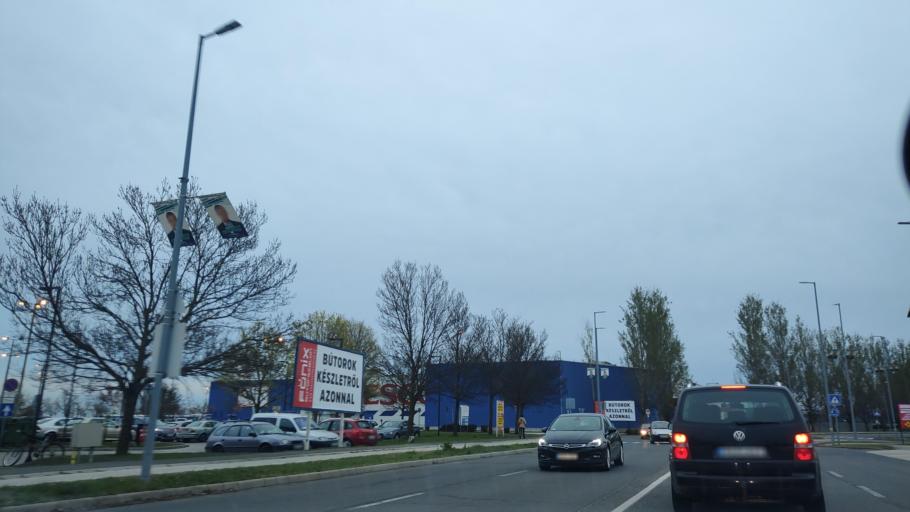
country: HU
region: Vas
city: Szombathely
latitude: 47.2409
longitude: 16.6513
